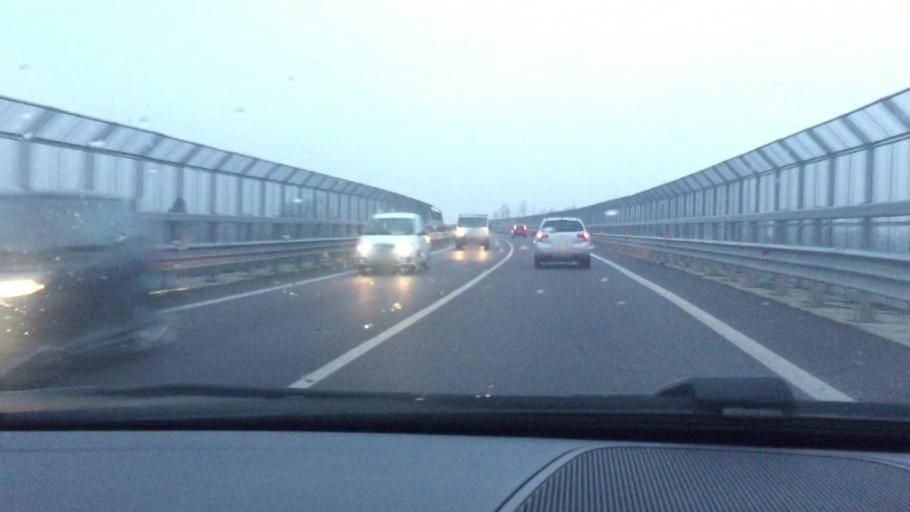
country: IT
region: Veneto
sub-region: Provincia di Padova
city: Piove di Sacco-Piovega
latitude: 45.3066
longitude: 12.0441
